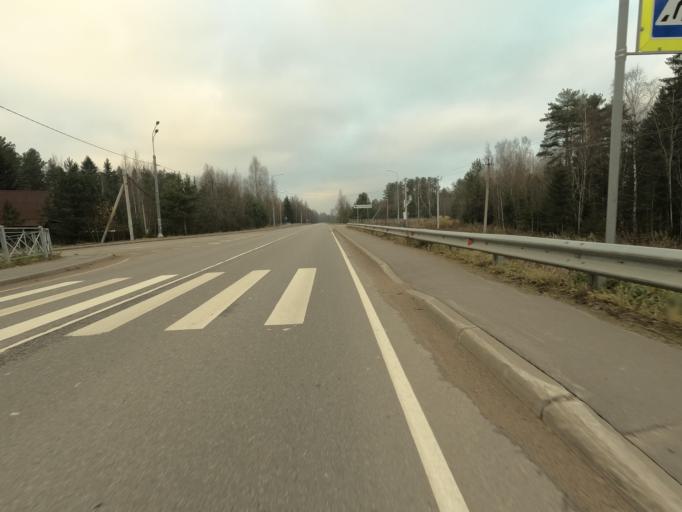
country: RU
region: Leningrad
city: Pavlovo
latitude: 59.8043
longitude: 30.9550
